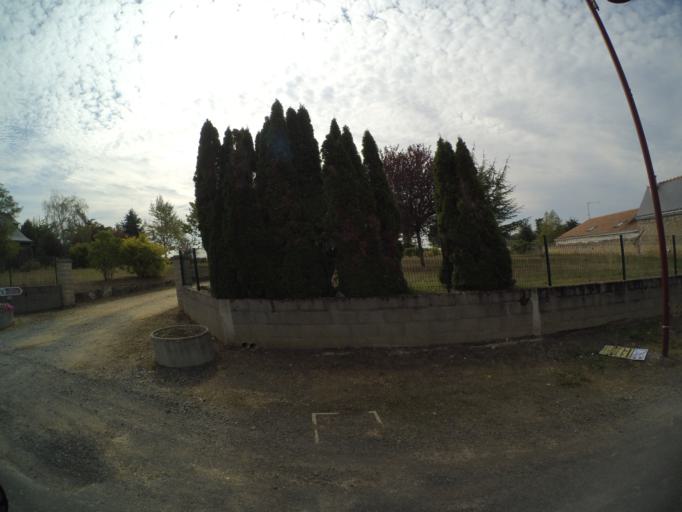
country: FR
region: Pays de la Loire
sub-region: Departement de Maine-et-Loire
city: Martigne-Briand
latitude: 47.2002
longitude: -0.4245
